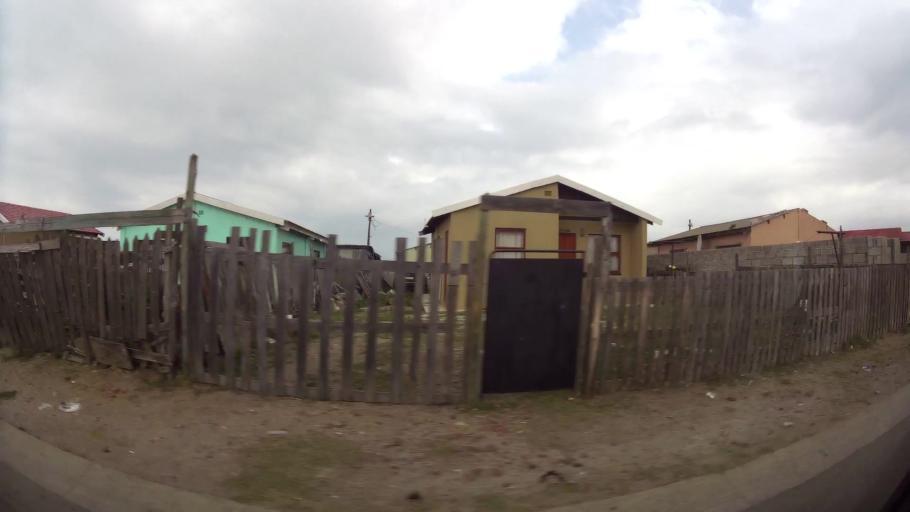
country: ZA
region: Eastern Cape
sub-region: Nelson Mandela Bay Metropolitan Municipality
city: Port Elizabeth
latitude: -33.8959
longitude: 25.6067
